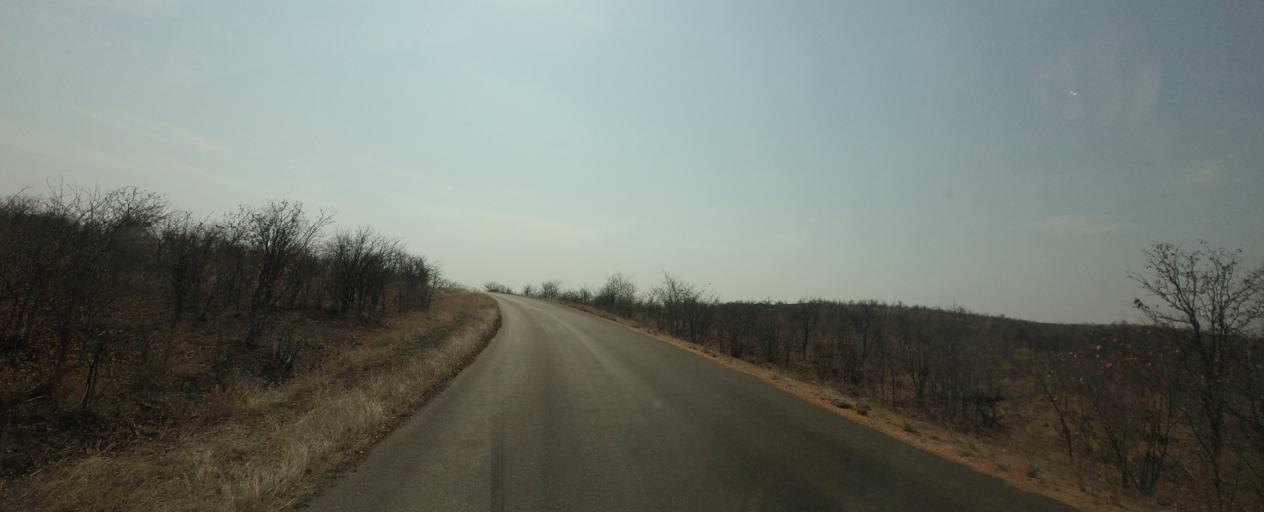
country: ZA
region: Limpopo
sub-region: Mopani District Municipality
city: Phalaborwa
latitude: -23.9713
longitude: 31.6331
